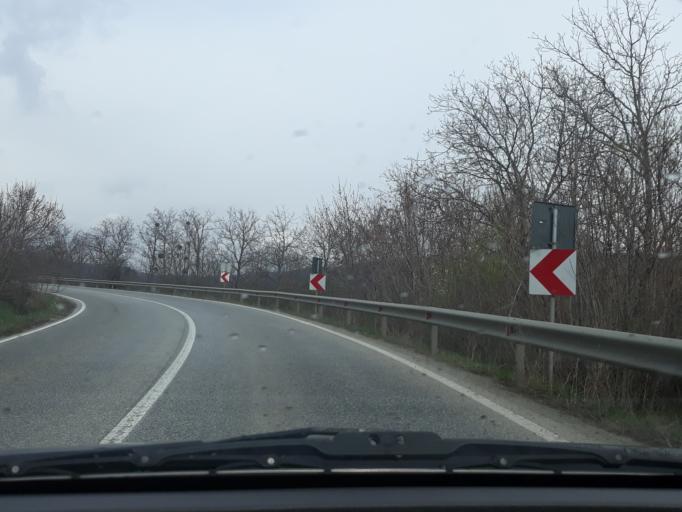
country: RO
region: Harghita
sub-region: Comuna Lupeni
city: Lupeni
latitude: 46.3969
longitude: 25.2144
